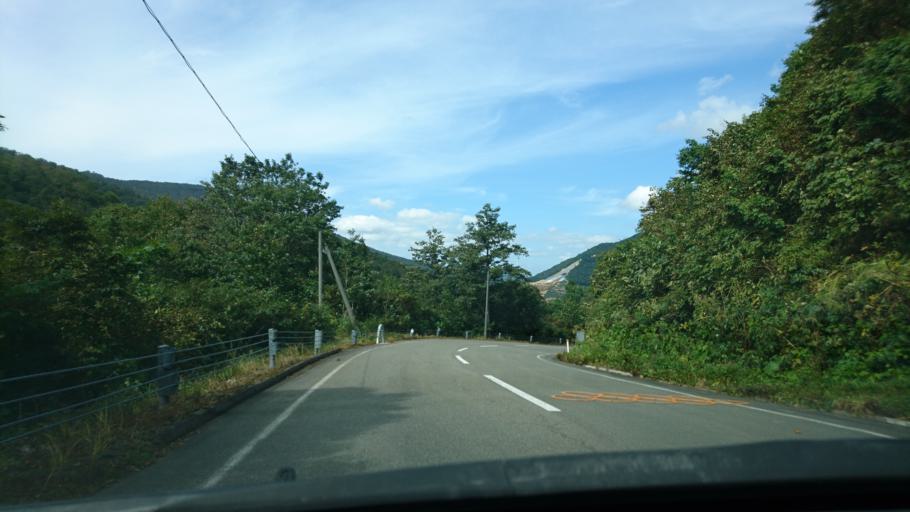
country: JP
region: Akita
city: Yuzawa
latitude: 39.0214
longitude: 140.7281
